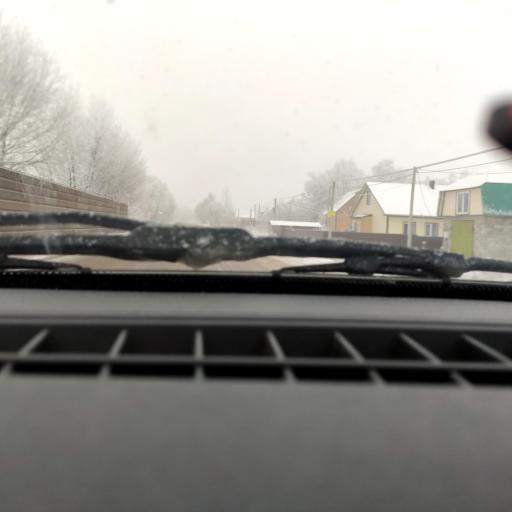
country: RU
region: Bashkortostan
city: Kabakovo
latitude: 54.6978
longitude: 56.1310
